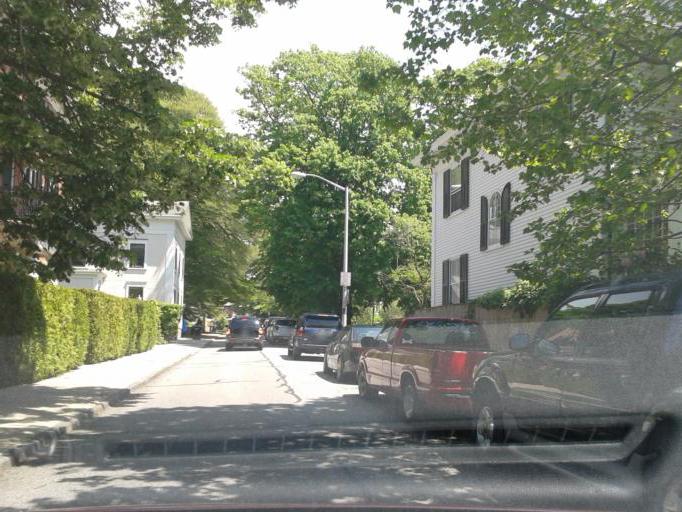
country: US
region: Rhode Island
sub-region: Newport County
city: Newport
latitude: 41.4864
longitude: -71.3109
